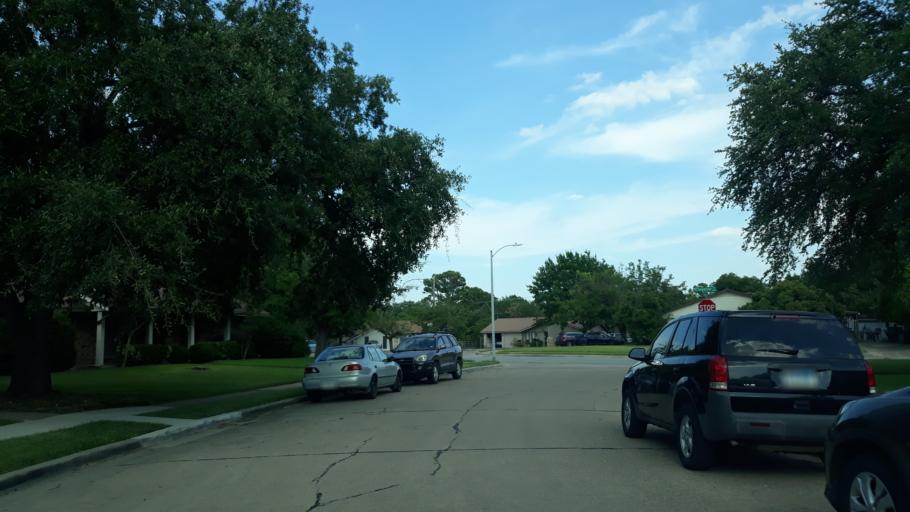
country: US
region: Texas
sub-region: Dallas County
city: Irving
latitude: 32.8484
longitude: -97.0016
